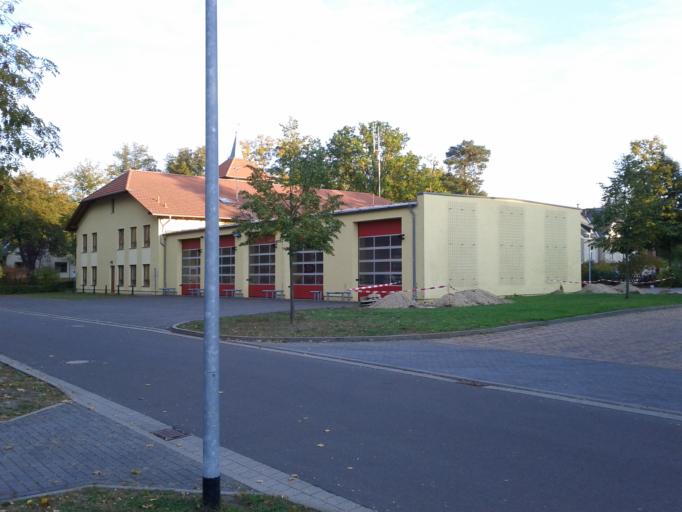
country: DE
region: Brandenburg
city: Schoneiche
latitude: 52.4670
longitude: 13.6972
